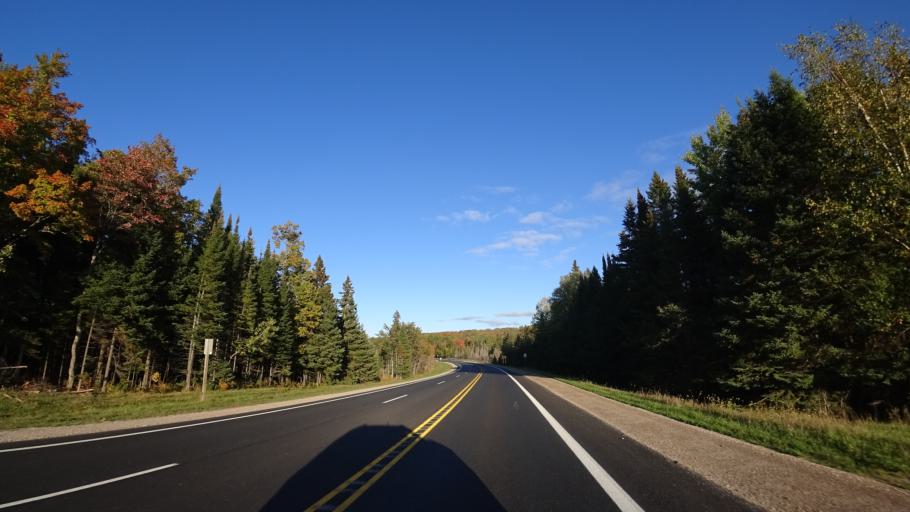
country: US
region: Michigan
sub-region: Luce County
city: Newberry
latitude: 46.3358
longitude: -85.7564
